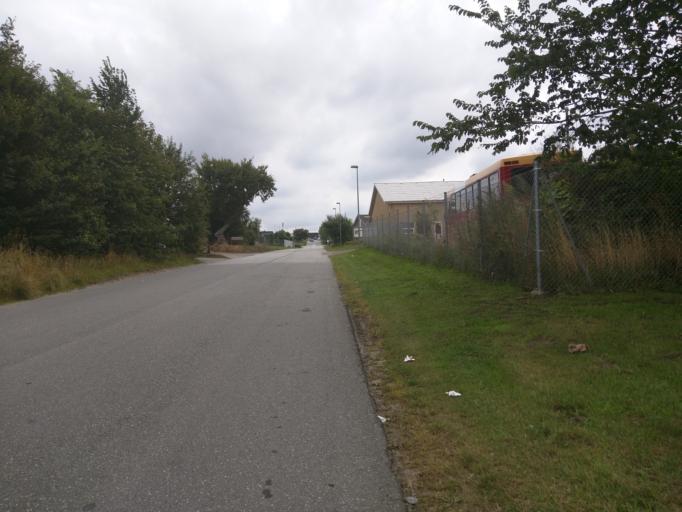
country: DK
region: Central Jutland
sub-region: Viborg Kommune
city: Viborg
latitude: 56.4509
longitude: 9.3648
